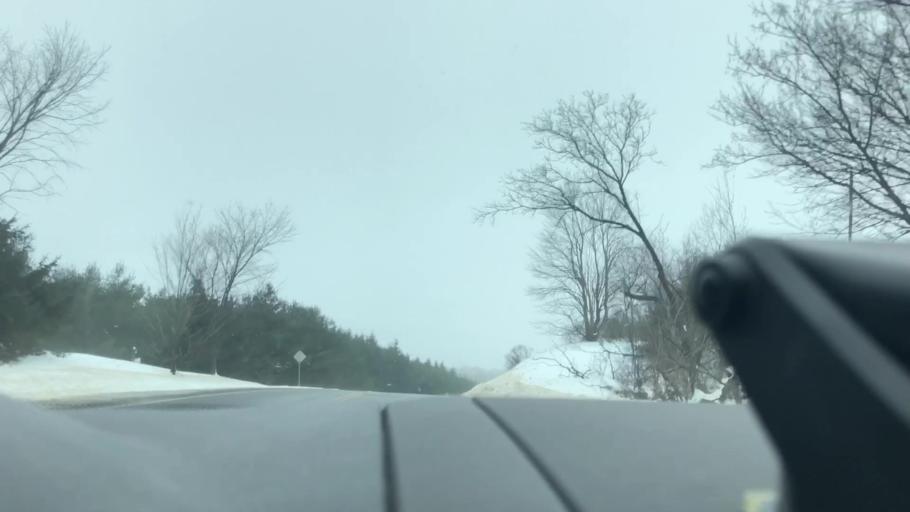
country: US
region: Michigan
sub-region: Charlevoix County
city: East Jordan
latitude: 45.1576
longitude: -85.1602
